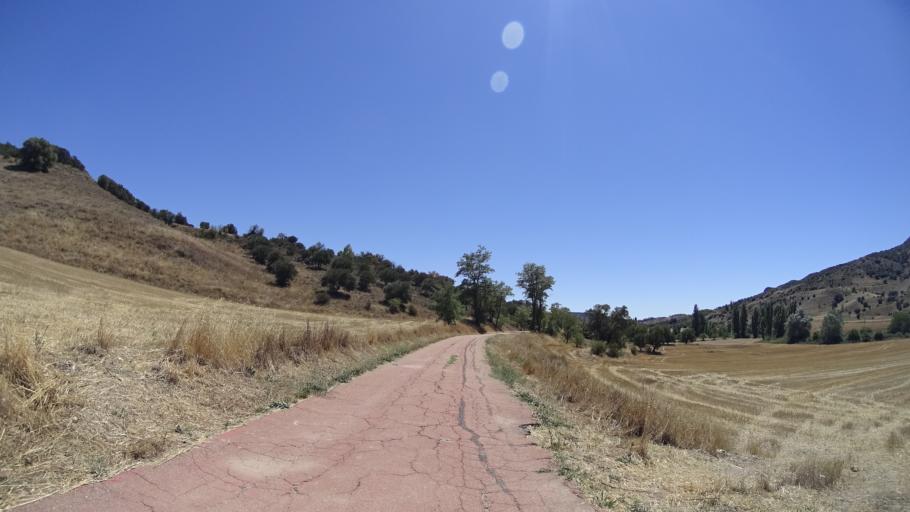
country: ES
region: Madrid
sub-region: Provincia de Madrid
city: Ambite
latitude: 40.3047
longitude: -3.1918
